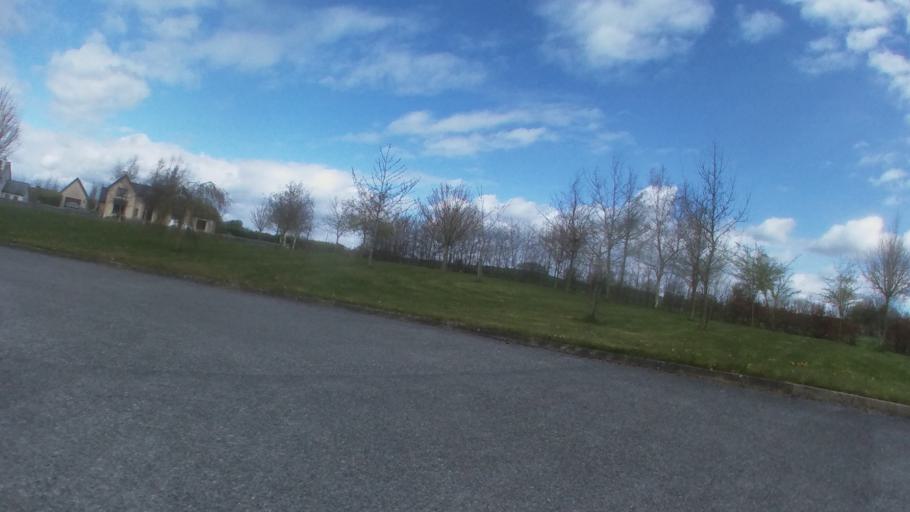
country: IE
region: Leinster
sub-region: Kilkenny
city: Kilkenny
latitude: 52.7183
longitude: -7.2333
